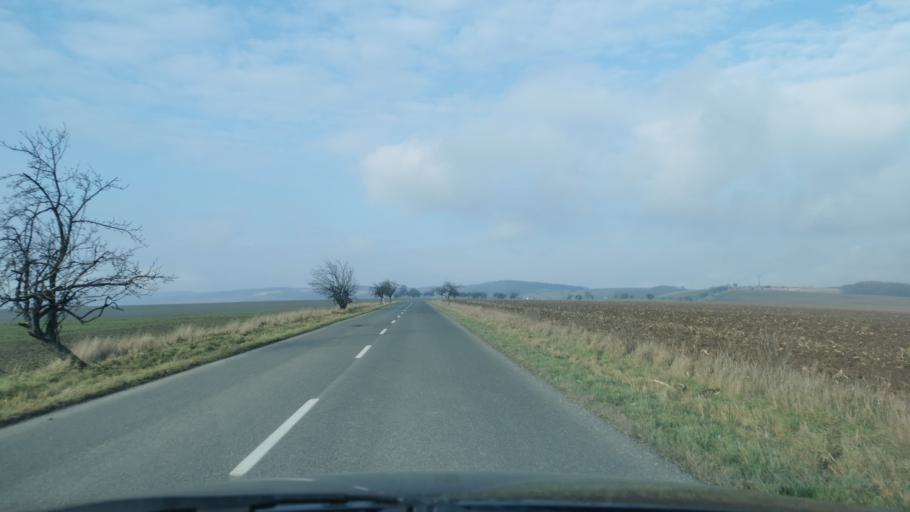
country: SK
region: Trnavsky
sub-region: Okres Senica
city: Senica
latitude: 48.7148
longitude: 17.3264
